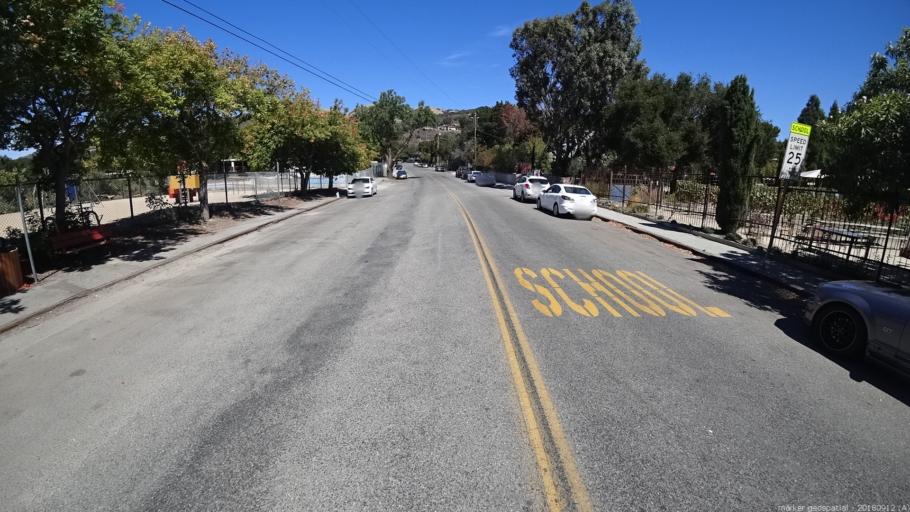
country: US
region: California
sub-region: Monterey County
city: Carmel Valley Village
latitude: 36.4811
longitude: -121.7335
